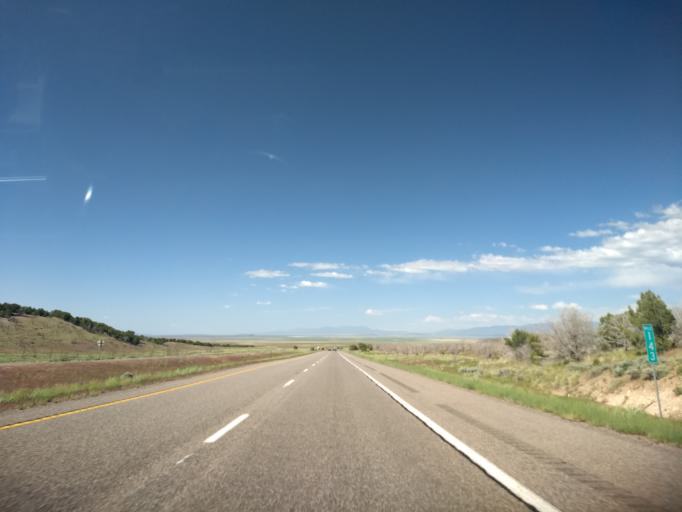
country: US
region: Utah
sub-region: Millard County
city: Fillmore
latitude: 38.7246
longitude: -112.5947
